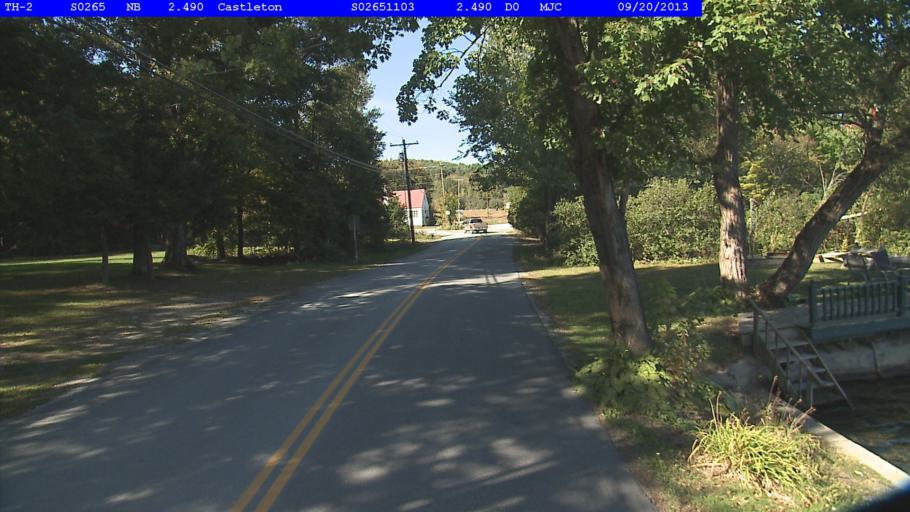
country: US
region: Vermont
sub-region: Rutland County
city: Fair Haven
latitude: 43.6374
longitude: -73.2321
